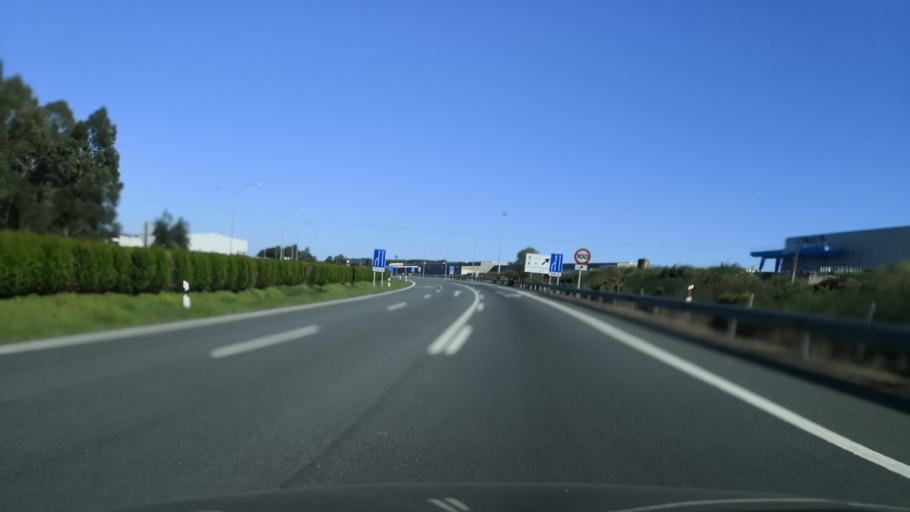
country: ES
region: Galicia
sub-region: Provincia da Coruna
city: Coiros
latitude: 43.2405
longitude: -8.1405
